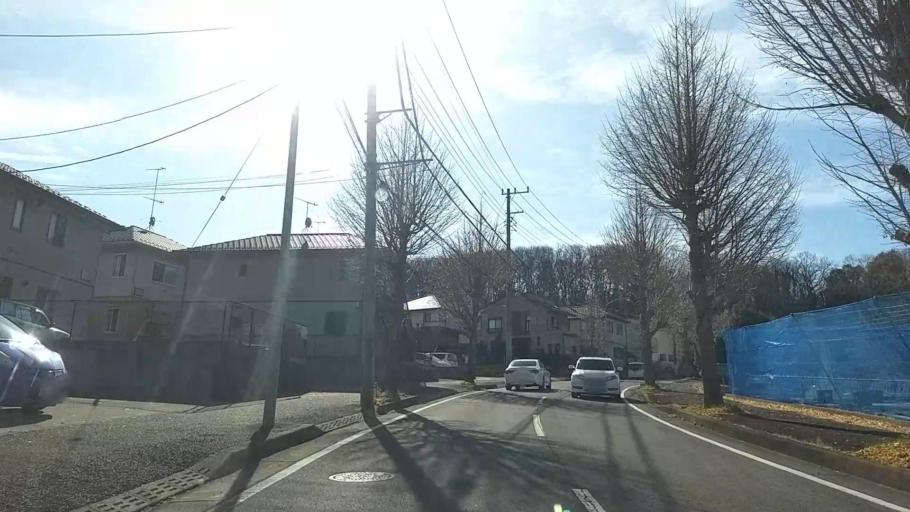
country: JP
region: Kanagawa
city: Hadano
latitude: 35.3607
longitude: 139.2270
